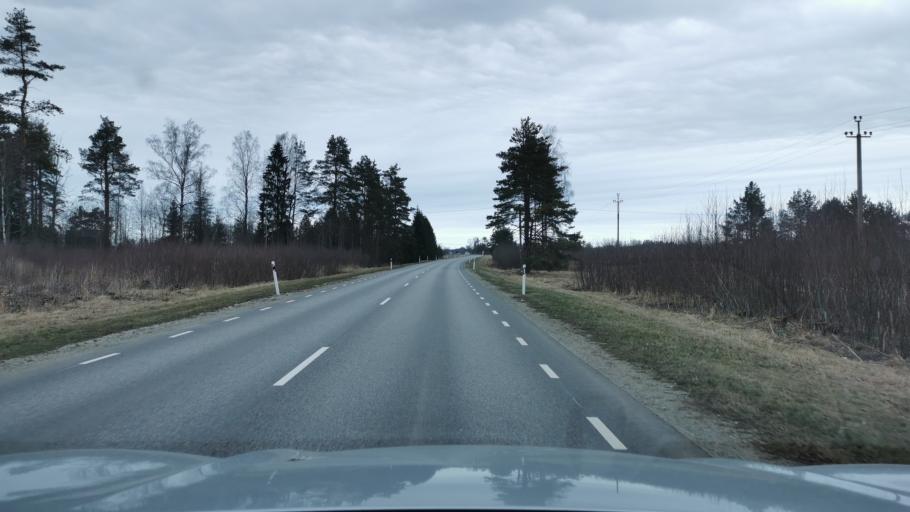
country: EE
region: Ida-Virumaa
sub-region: Puessi linn
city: Pussi
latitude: 59.3637
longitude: 27.0274
